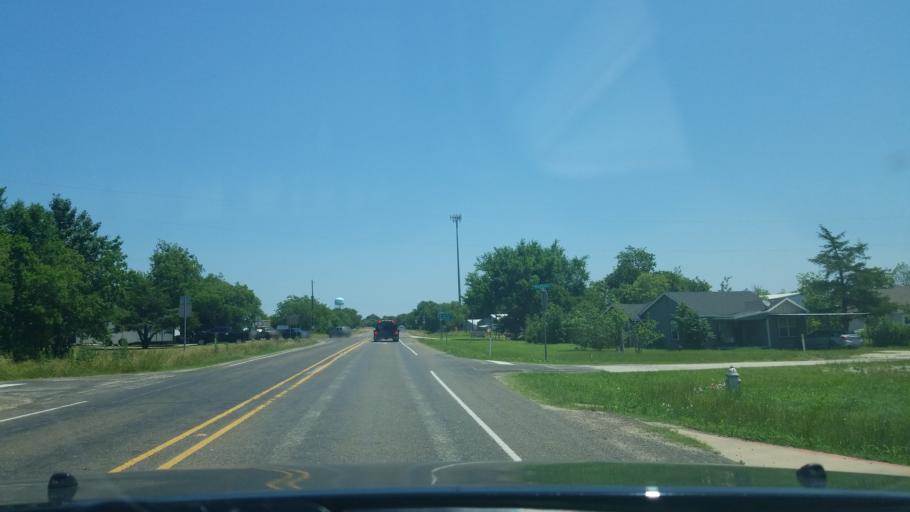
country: US
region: Texas
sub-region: Denton County
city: Krum
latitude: 33.2649
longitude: -97.2363
